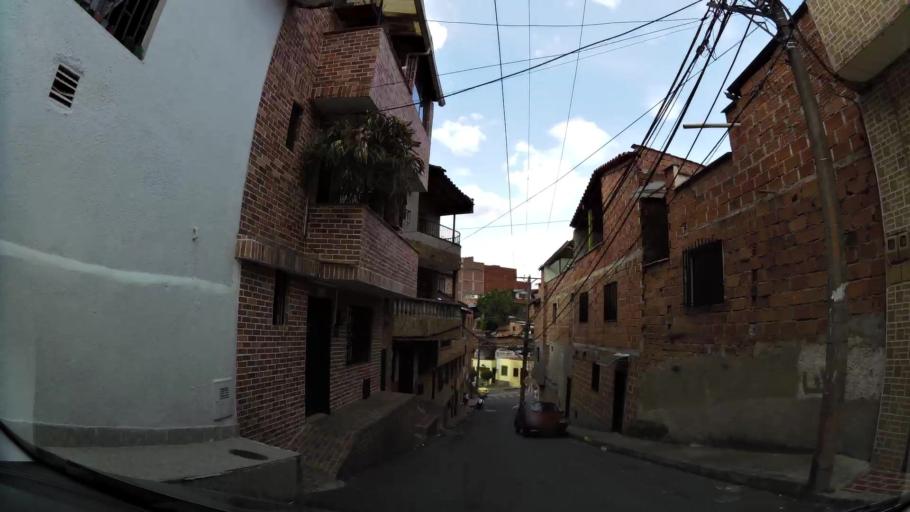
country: CO
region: Antioquia
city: Envigado
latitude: 6.1594
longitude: -75.5820
